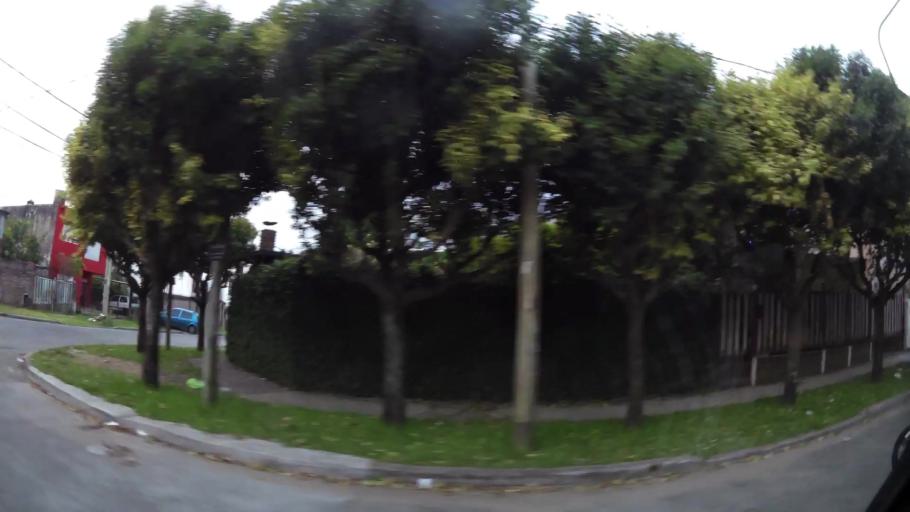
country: AR
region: Buenos Aires
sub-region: Partido de Quilmes
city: Quilmes
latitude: -34.7430
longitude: -58.2460
